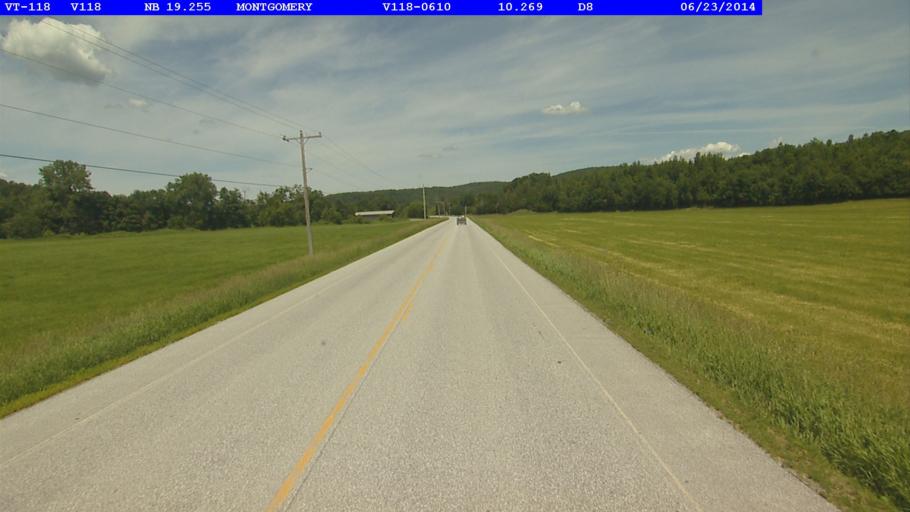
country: US
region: Vermont
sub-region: Franklin County
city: Richford
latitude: 44.9177
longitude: -72.6702
